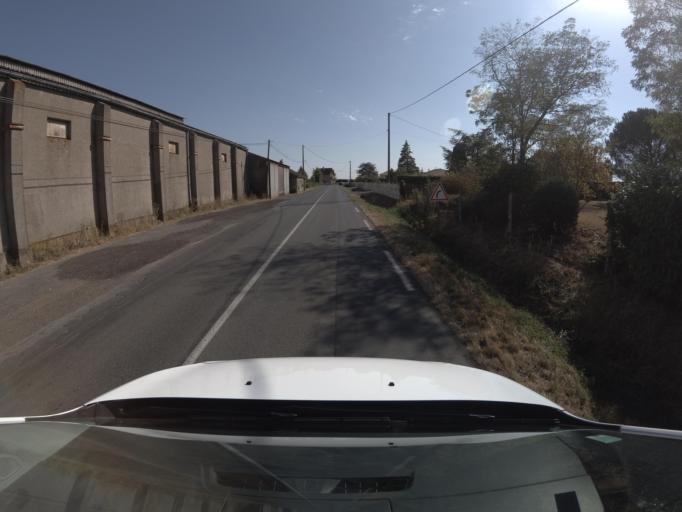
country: FR
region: Poitou-Charentes
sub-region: Departement des Deux-Sevres
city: Argenton-les-Vallees
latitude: 46.9924
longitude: -0.4336
